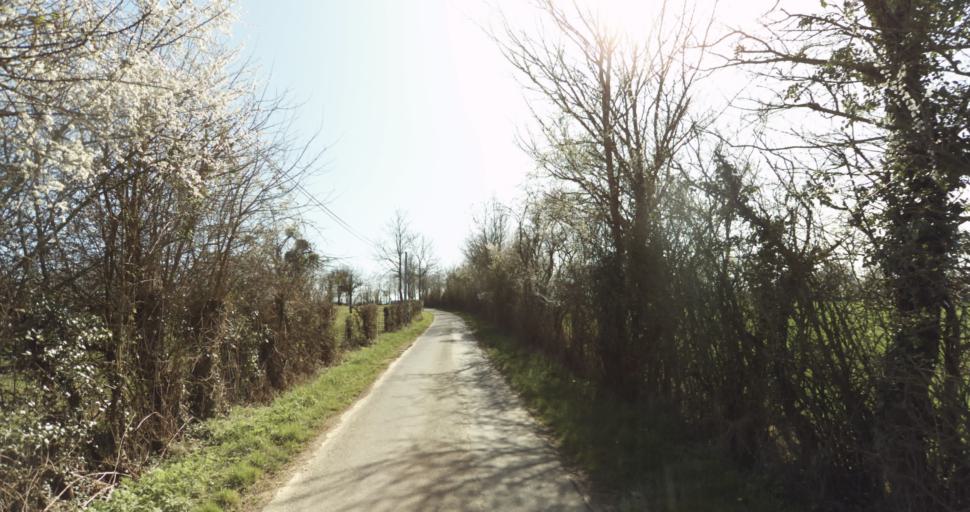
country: FR
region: Lower Normandy
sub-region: Departement du Calvados
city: Saint-Pierre-sur-Dives
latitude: 48.9425
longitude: -0.0069
